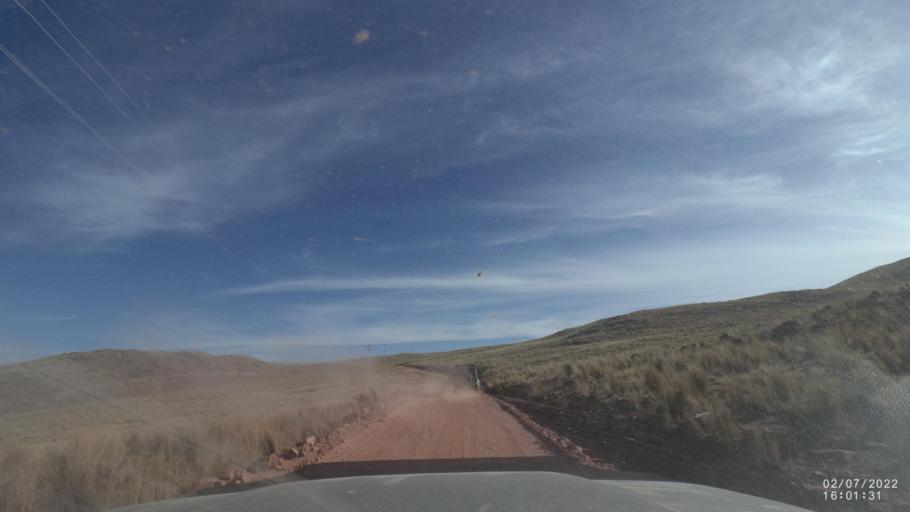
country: BO
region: Cochabamba
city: Irpa Irpa
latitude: -17.9070
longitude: -66.4386
